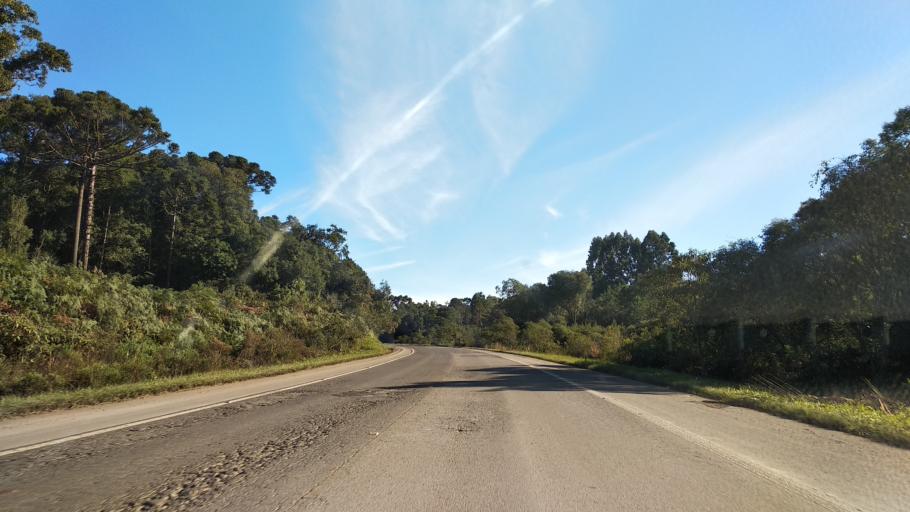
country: BR
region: Santa Catarina
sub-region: Campos Novos
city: Campos Novos
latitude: -27.4005
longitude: -51.2007
